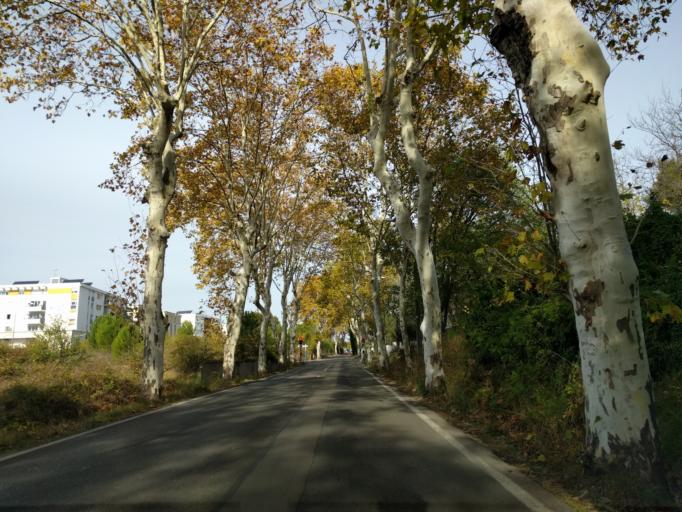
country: FR
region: Languedoc-Roussillon
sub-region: Departement de l'Herault
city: Montferrier-sur-Lez
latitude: 43.6357
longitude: 3.8488
